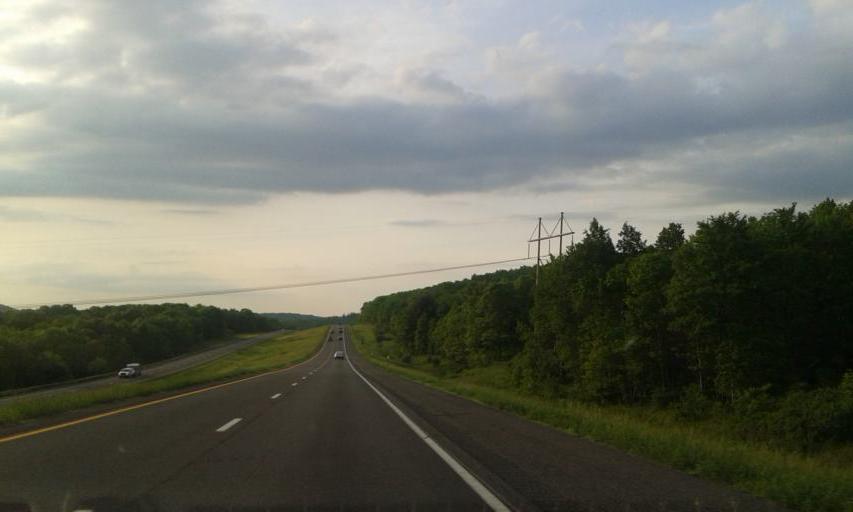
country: US
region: New York
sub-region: Broome County
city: Chenango Bridge
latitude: 42.2081
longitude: -75.9001
